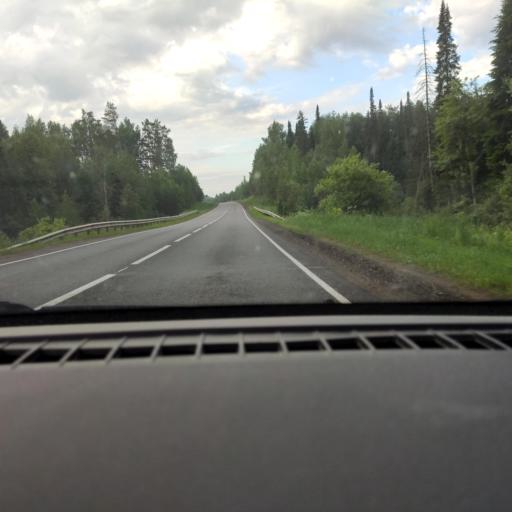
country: RU
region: Udmurtiya
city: Votkinsk
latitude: 57.1869
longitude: 54.1589
